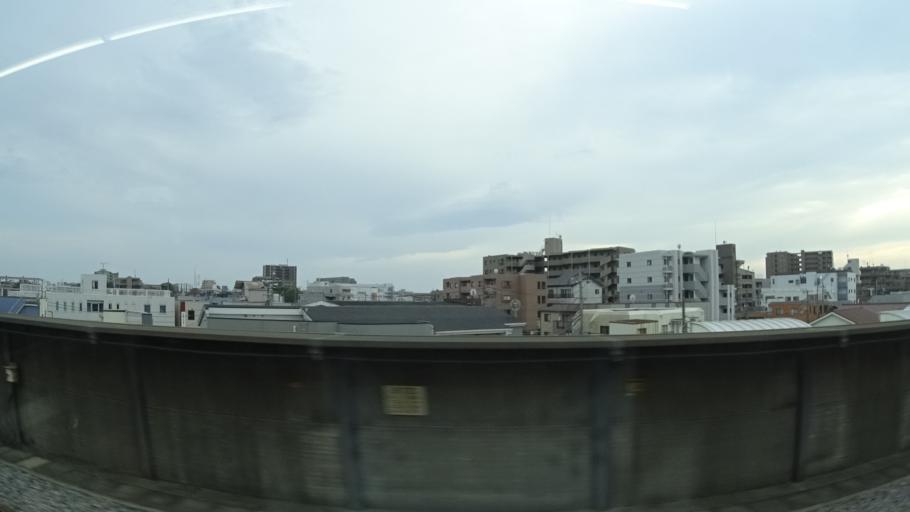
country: JP
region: Saitama
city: Shimotoda
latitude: 35.8119
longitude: 139.6733
